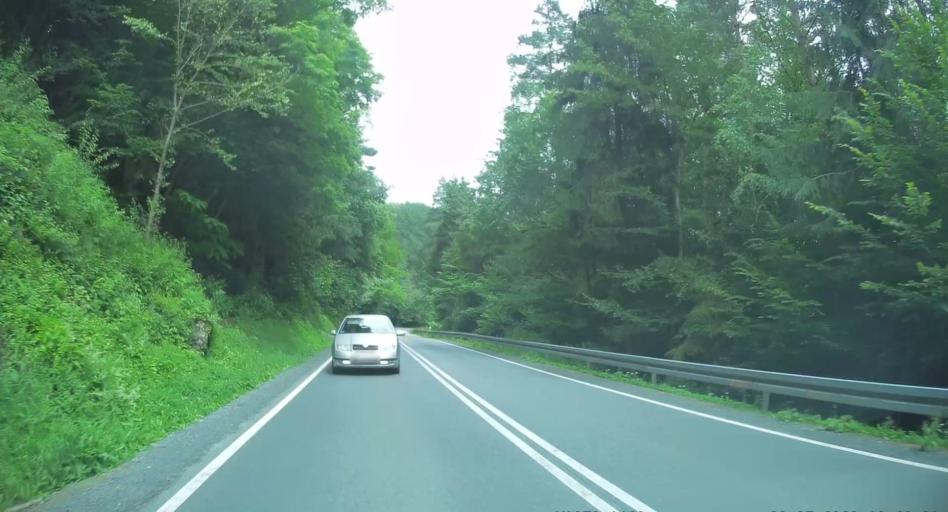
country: PL
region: Lesser Poland Voivodeship
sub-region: Powiat nowosadecki
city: Muszyna
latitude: 49.3480
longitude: 20.8066
